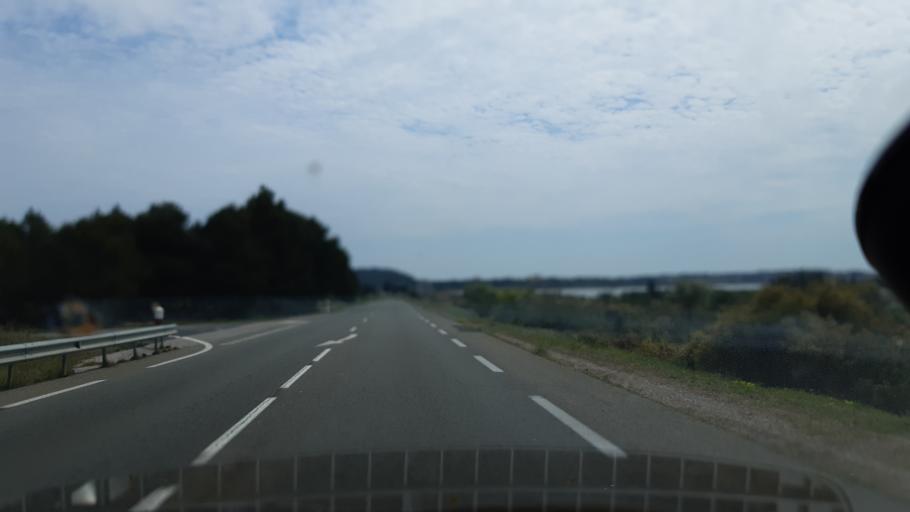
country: FR
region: Languedoc-Roussillon
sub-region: Departement de l'Aude
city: Gruissan
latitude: 43.1199
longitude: 3.0836
